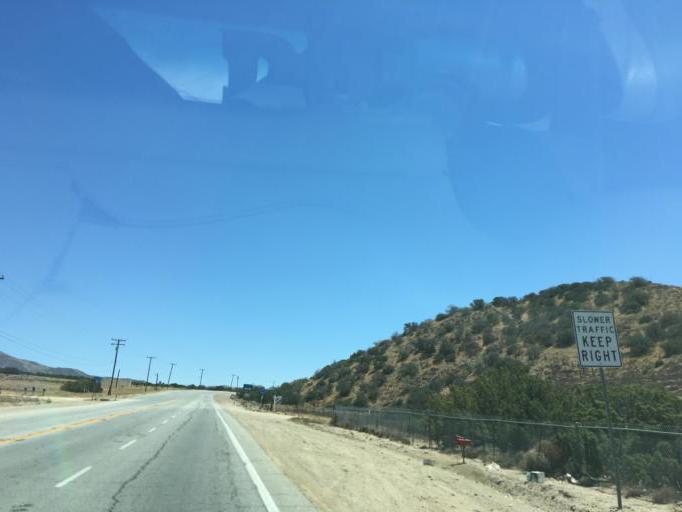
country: US
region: California
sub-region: Los Angeles County
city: Acton
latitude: 34.5220
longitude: -118.2524
